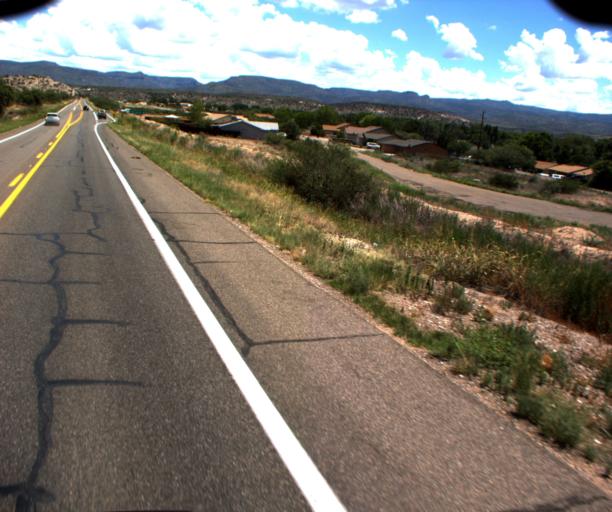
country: US
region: Arizona
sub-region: Yavapai County
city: Camp Verde
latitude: 34.5285
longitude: -111.7962
